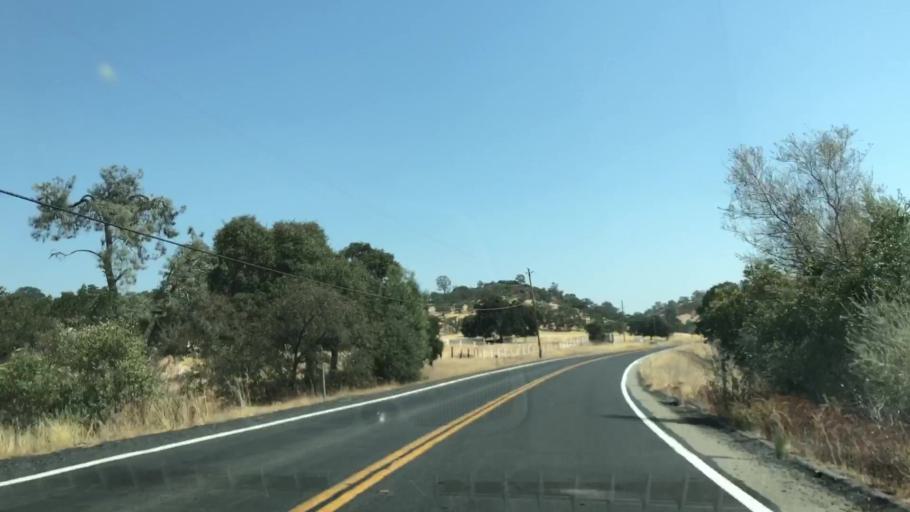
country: US
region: California
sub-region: Tuolumne County
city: Jamestown
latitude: 37.8883
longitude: -120.5187
